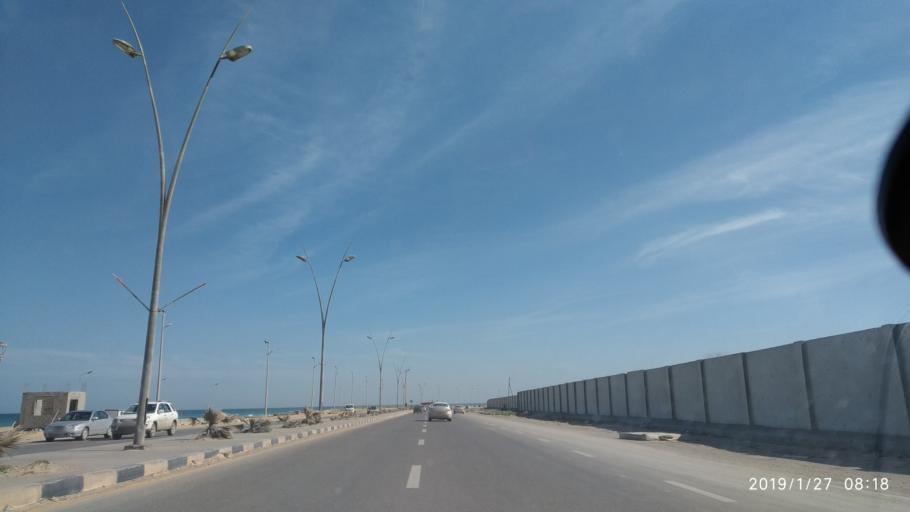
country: LY
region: Tripoli
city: Tagiura
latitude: 32.9085
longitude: 13.2842
